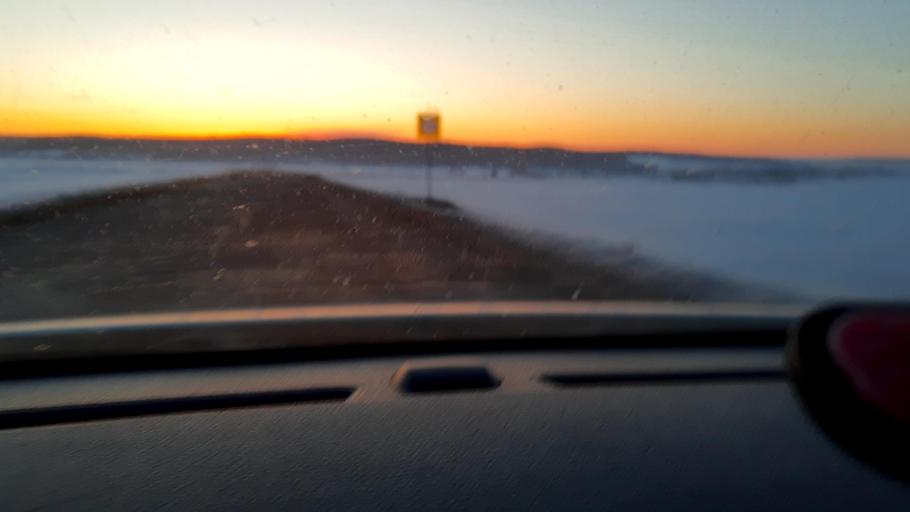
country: RU
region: Bashkortostan
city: Avdon
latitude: 54.3882
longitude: 55.7795
